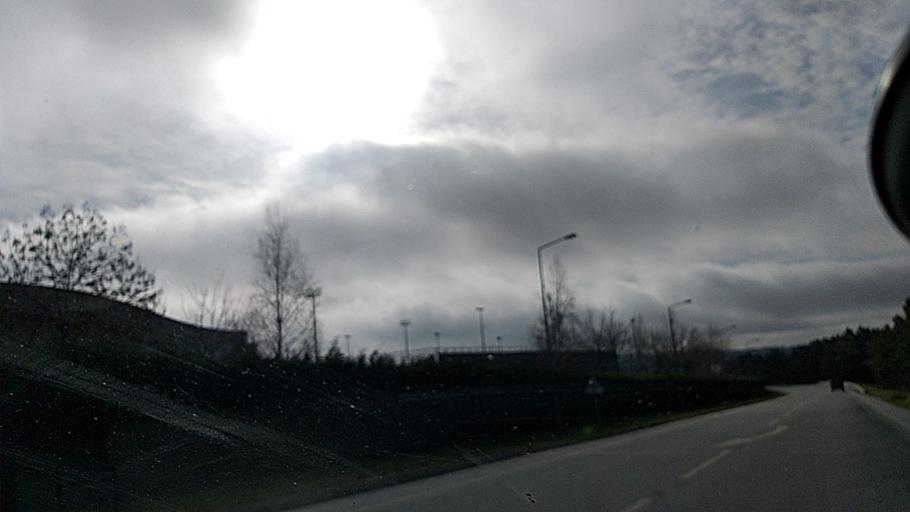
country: PT
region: Guarda
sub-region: Aguiar da Beira
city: Aguiar da Beira
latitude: 40.8147
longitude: -7.5368
